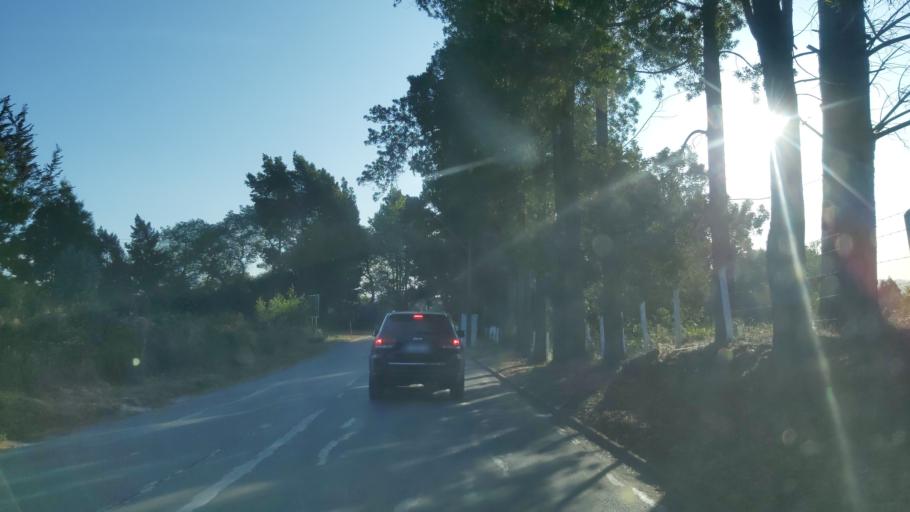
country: CL
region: Biobio
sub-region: Provincia de Concepcion
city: Tome
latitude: -36.5389
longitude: -72.9282
